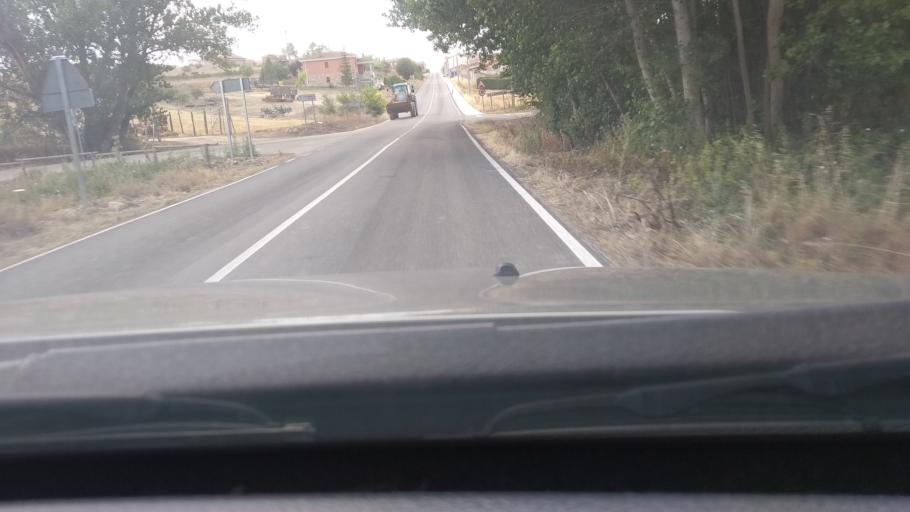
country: ES
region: Castille and Leon
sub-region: Provincia de Burgos
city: Villafruela
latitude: 41.9194
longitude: -3.9075
